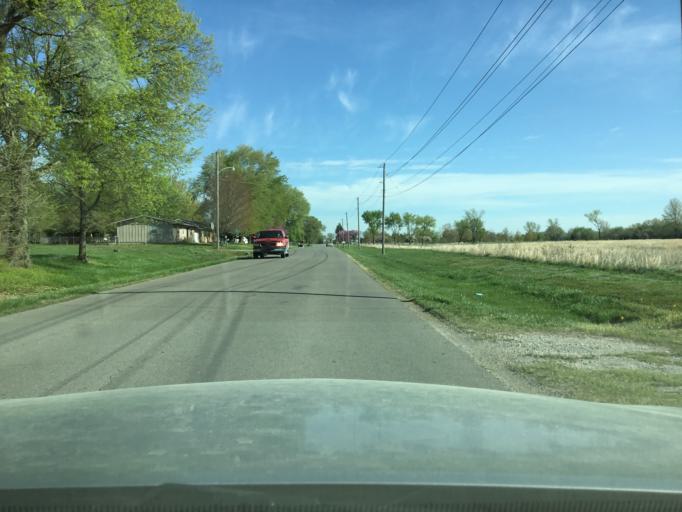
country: US
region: Kansas
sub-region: Neosho County
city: Chanute
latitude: 37.6612
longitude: -95.4435
